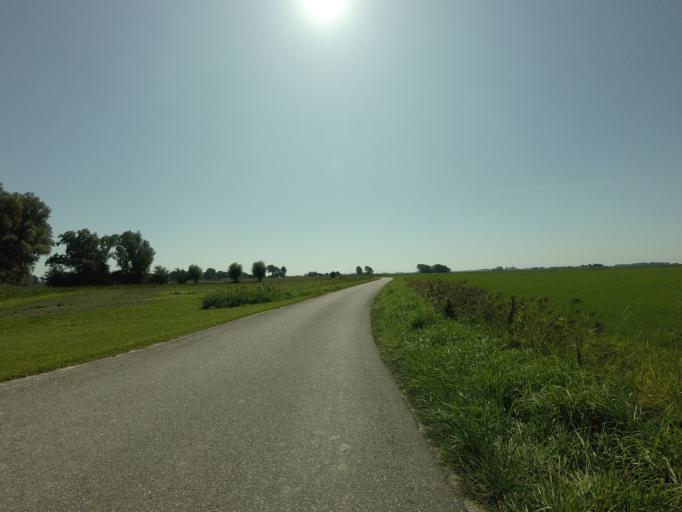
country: NL
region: Friesland
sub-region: Gemeente Dongeradeel
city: Ternaard
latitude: 53.3846
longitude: 6.0286
